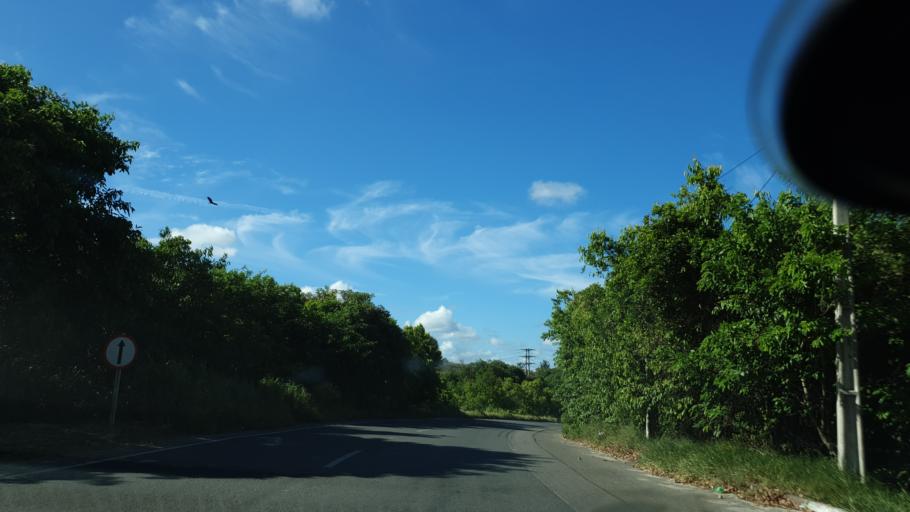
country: BR
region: Bahia
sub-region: Camacari
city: Camacari
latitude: -12.6817
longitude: -38.3021
